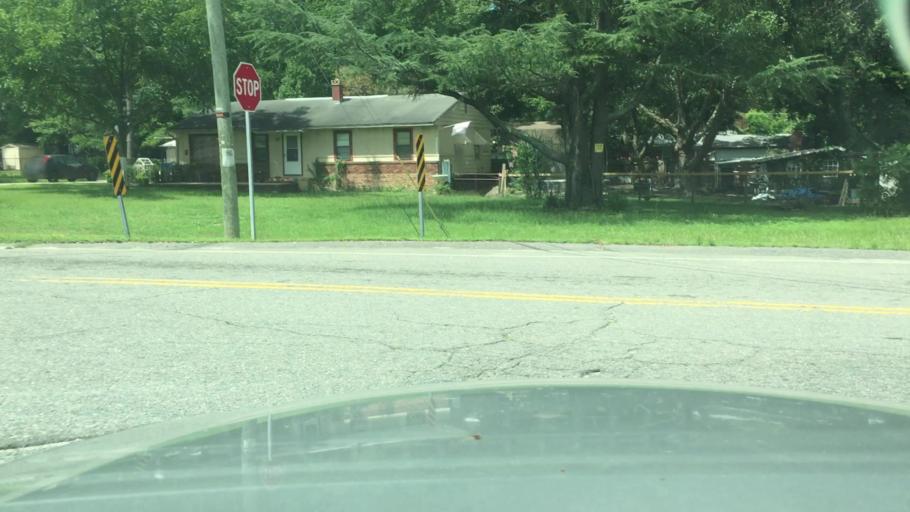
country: US
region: North Carolina
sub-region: Cumberland County
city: Hope Mills
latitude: 35.0195
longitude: -78.9352
